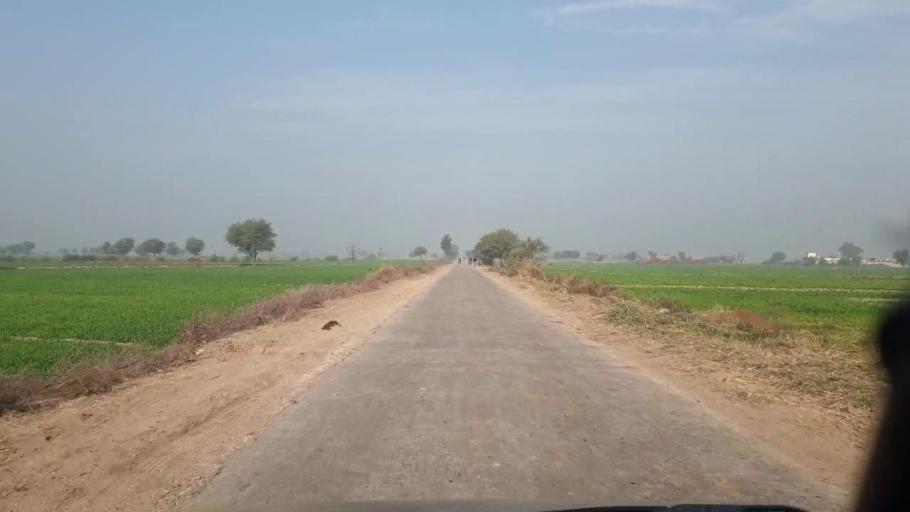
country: PK
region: Sindh
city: Shahdadpur
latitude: 25.9691
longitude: 68.5801
